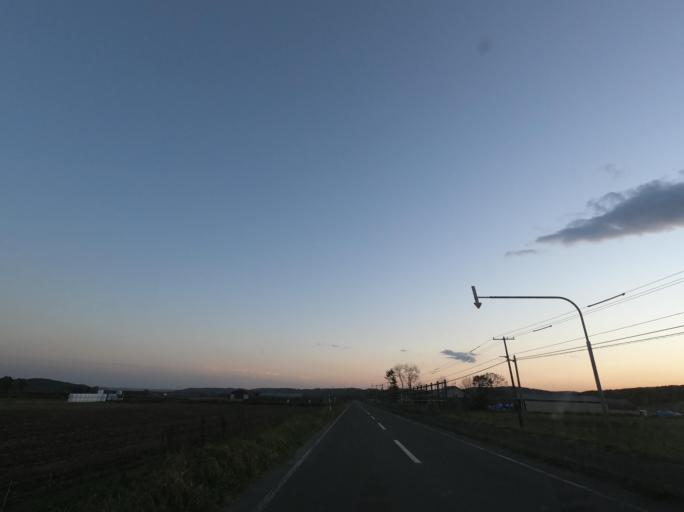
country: JP
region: Hokkaido
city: Kushiro
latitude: 43.2103
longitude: 144.4290
